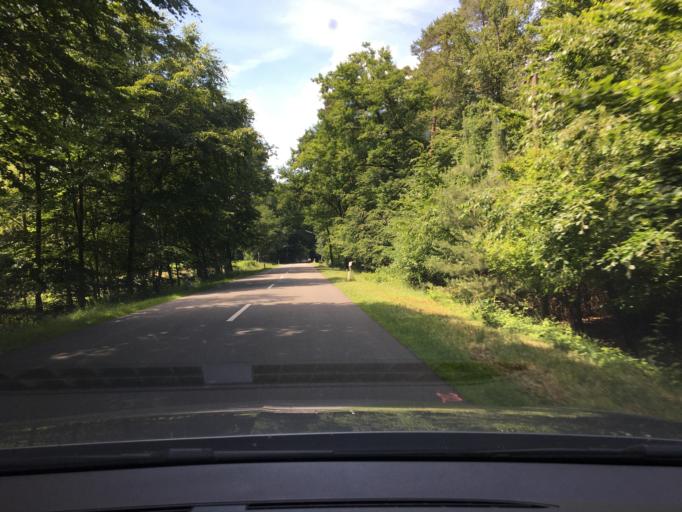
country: DE
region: Lower Saxony
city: Kirchtimke
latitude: 53.2489
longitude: 9.2137
